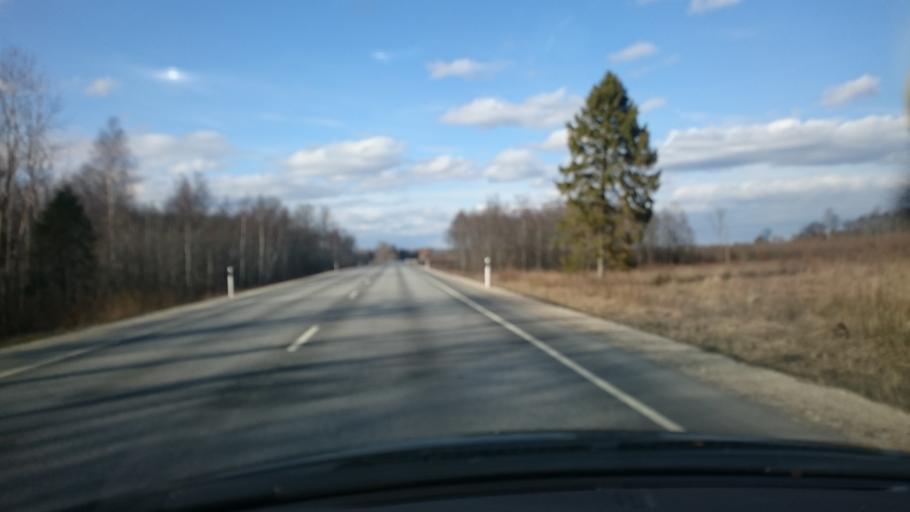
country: EE
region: Laeaene
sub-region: Lihula vald
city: Lihula
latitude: 58.8050
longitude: 24.0487
